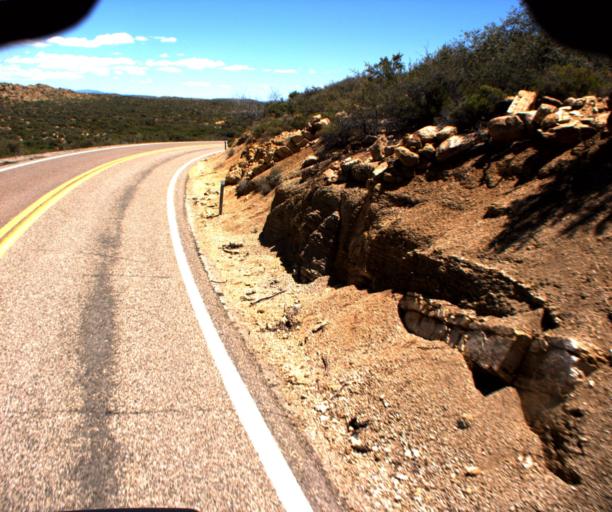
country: US
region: Arizona
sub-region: Yavapai County
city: Bagdad
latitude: 34.4445
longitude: -112.9395
